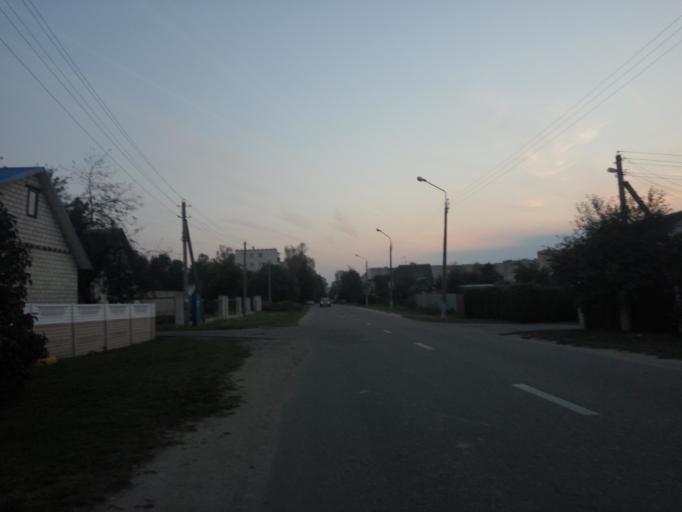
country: BY
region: Vitebsk
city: Vitebsk
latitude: 55.2029
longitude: 30.2442
